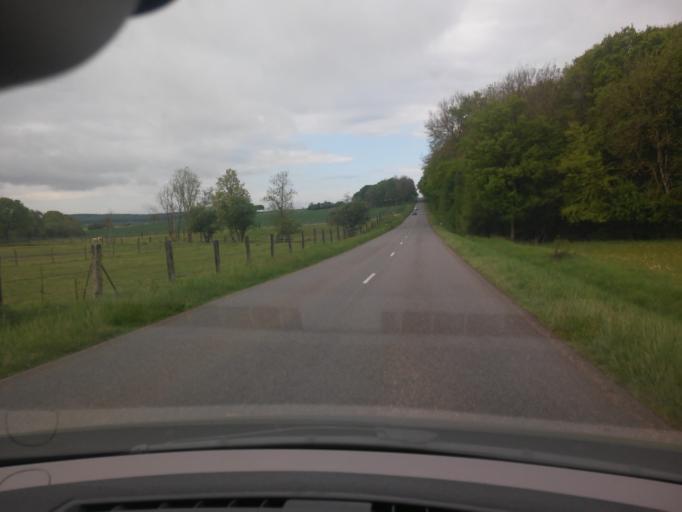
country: FR
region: Lorraine
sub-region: Departement de Meurthe-et-Moselle
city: Longuyon
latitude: 49.3962
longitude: 5.6198
